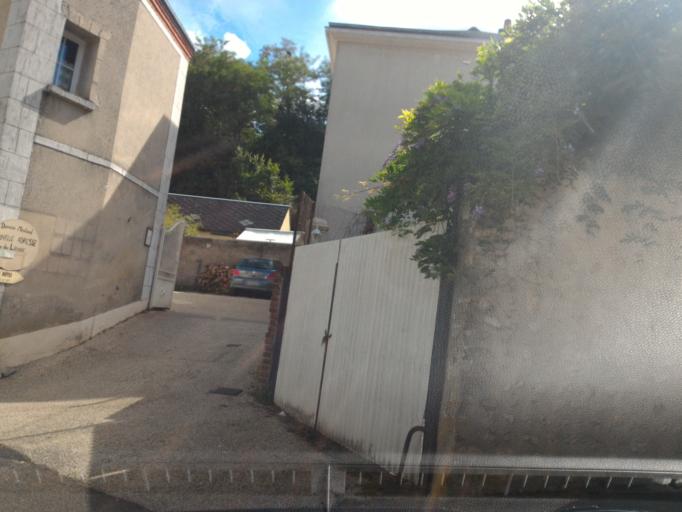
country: FR
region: Centre
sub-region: Departement d'Indre-et-Loire
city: Cangey
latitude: 47.4601
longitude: 1.0382
